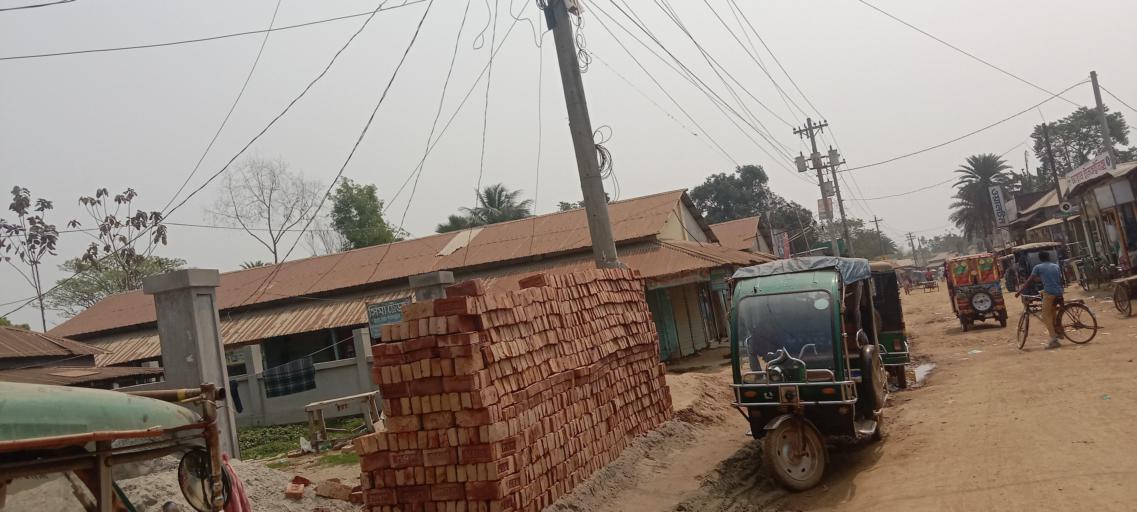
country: BD
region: Dhaka
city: Sakhipur
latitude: 24.3076
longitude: 90.2693
